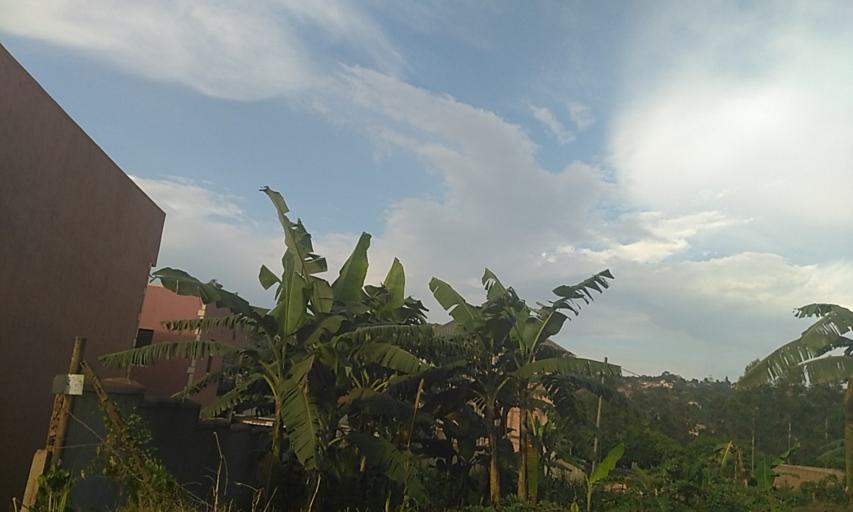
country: UG
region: Central Region
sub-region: Wakiso District
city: Kajansi
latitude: 0.2673
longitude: 32.5285
